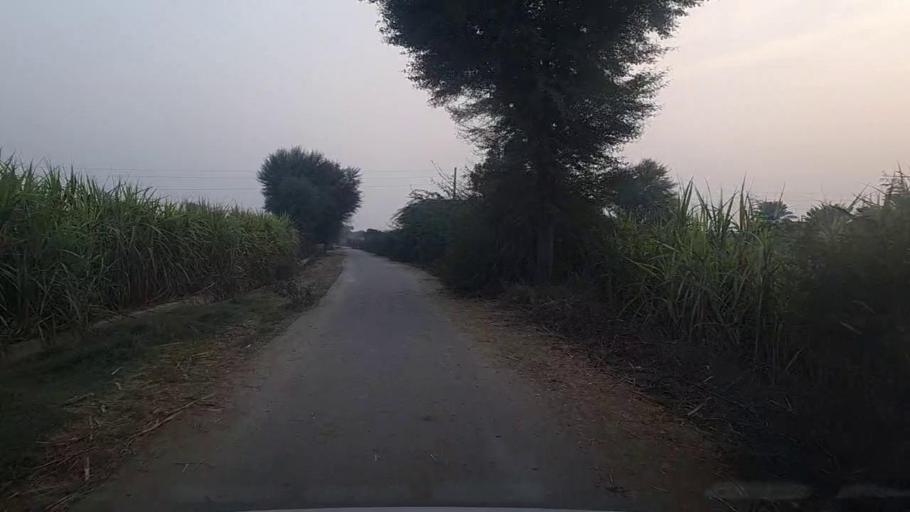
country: PK
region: Sindh
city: Kot Diji
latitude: 27.3438
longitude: 68.6426
